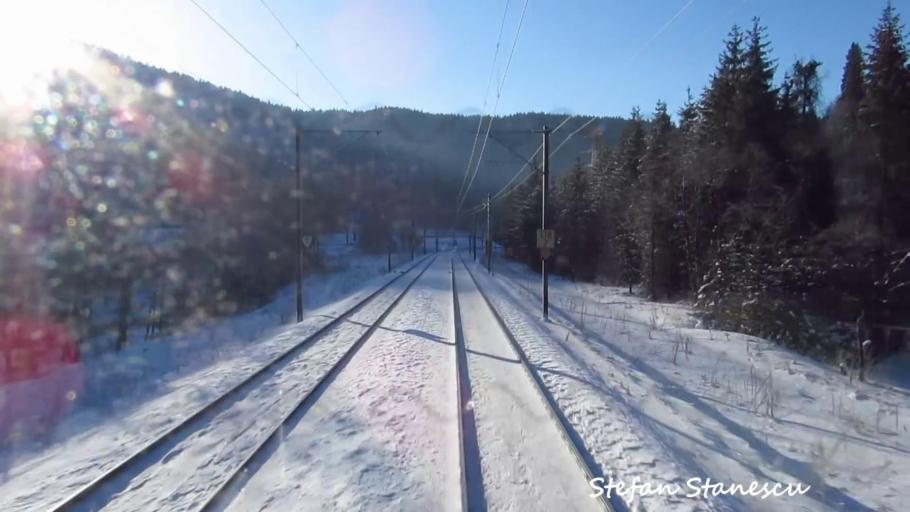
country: RO
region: Prahova
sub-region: Oras Azuga
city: Azuga
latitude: 45.4629
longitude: 25.5631
